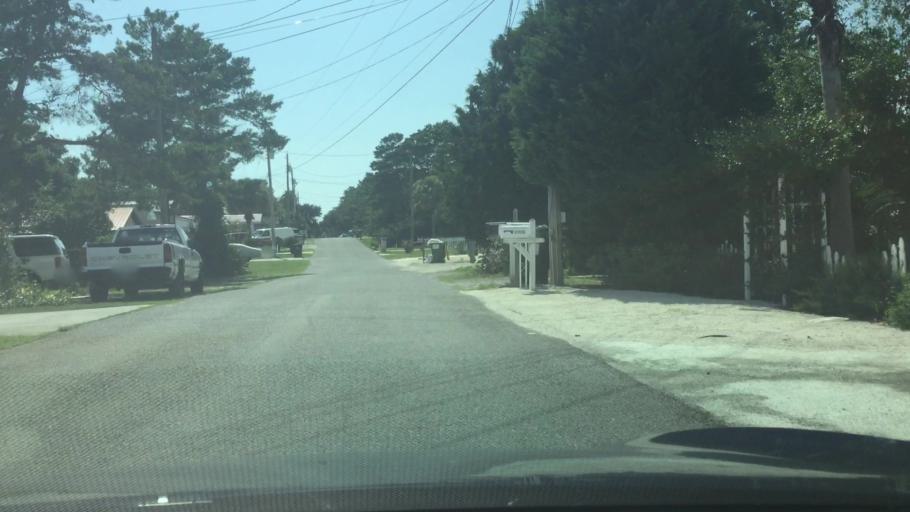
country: US
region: Florida
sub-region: Bay County
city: Laguna Beach
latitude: 30.2589
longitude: -85.9537
